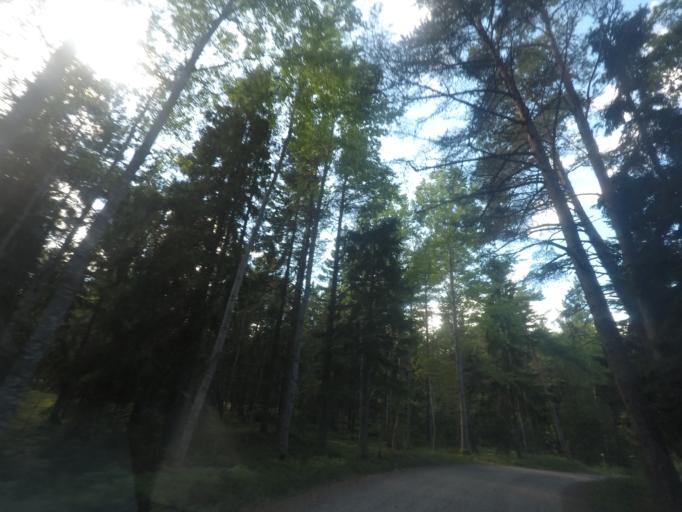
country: SE
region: Stockholm
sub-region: Norrtalje Kommun
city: Arno
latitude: 60.2083
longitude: 18.7347
